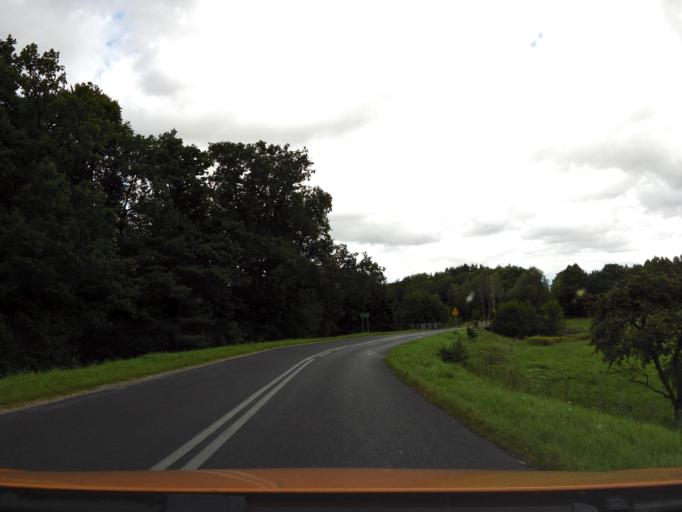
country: PL
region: West Pomeranian Voivodeship
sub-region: Powiat kolobrzeski
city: Goscino
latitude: 54.0593
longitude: 15.5528
